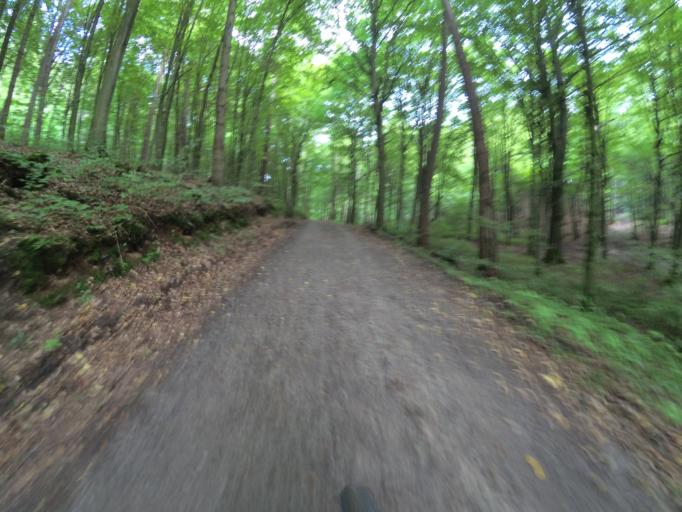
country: PL
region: Pomeranian Voivodeship
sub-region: Gdynia
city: Wielki Kack
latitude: 54.4893
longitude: 18.4547
